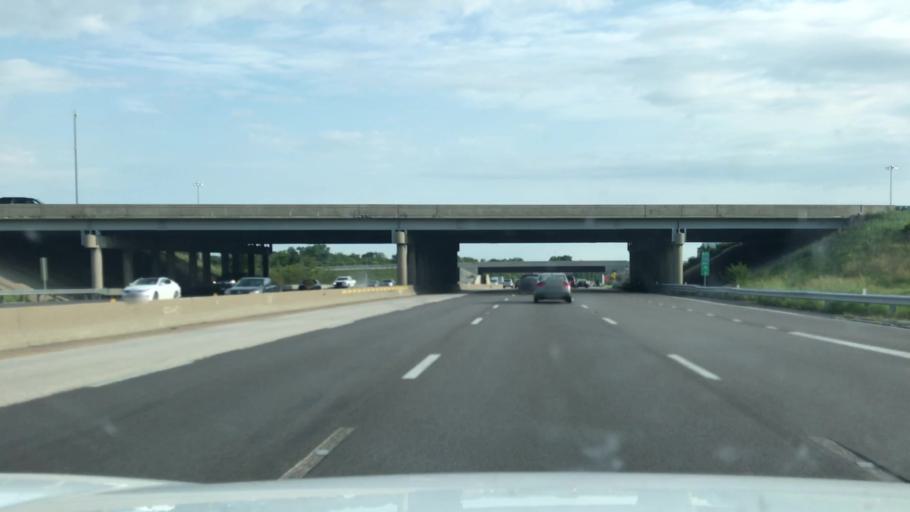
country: US
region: Missouri
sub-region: Saint Louis County
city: Maryland Heights
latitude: 38.6975
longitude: -90.4506
